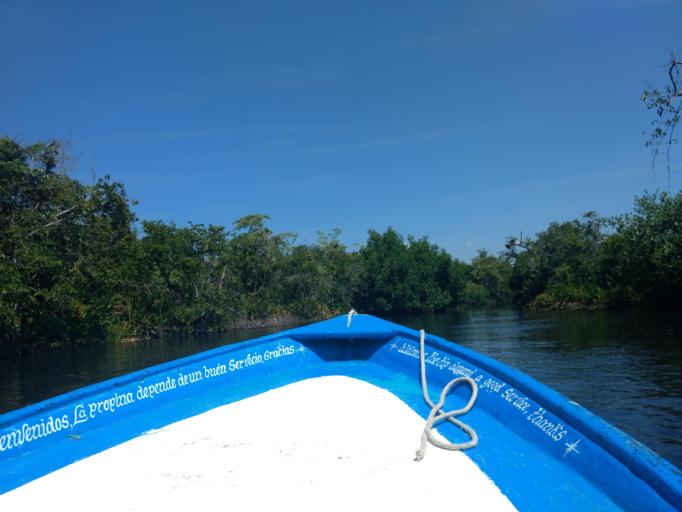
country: MX
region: Nayarit
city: San Blas
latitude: 21.5349
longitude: -105.2406
